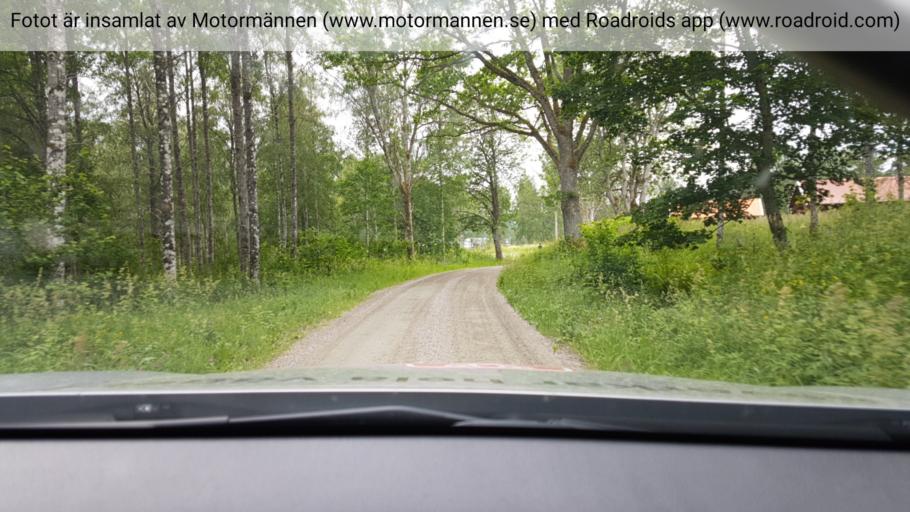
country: SE
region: Joenkoeping
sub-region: Mullsjo Kommun
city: Mullsjoe
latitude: 57.9102
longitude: 13.7664
